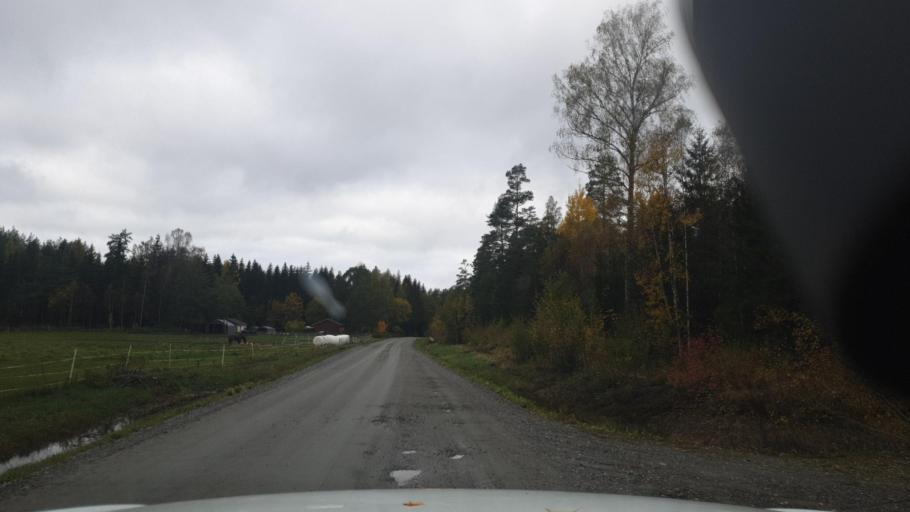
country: SE
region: Vaermland
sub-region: Karlstads Kommun
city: Edsvalla
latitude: 59.4498
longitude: 13.1525
